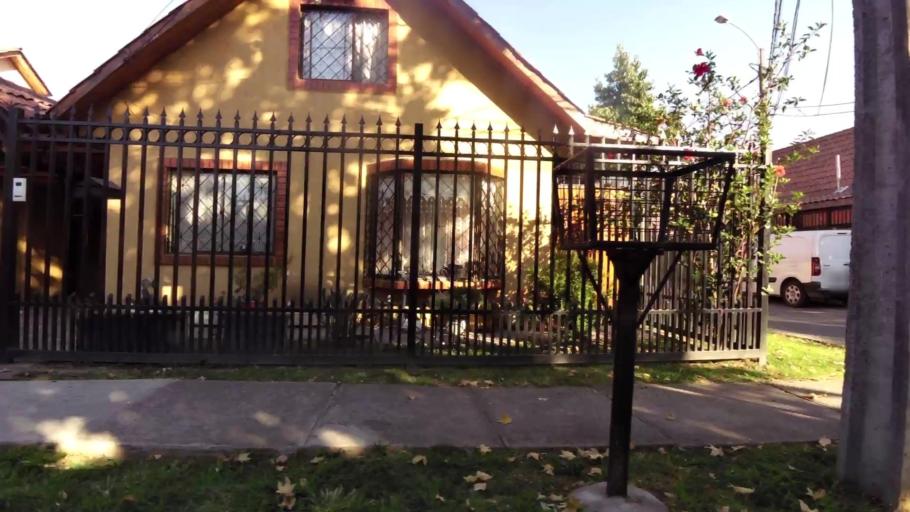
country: CL
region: Maule
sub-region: Provincia de Talca
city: Talca
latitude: -35.4398
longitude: -71.6867
